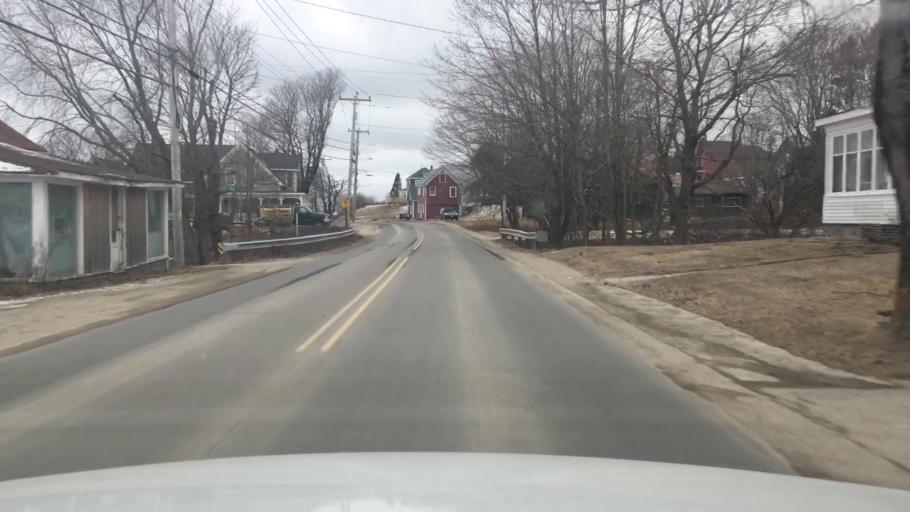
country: US
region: Maine
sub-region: Washington County
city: Jonesport
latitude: 44.5308
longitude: -67.6087
